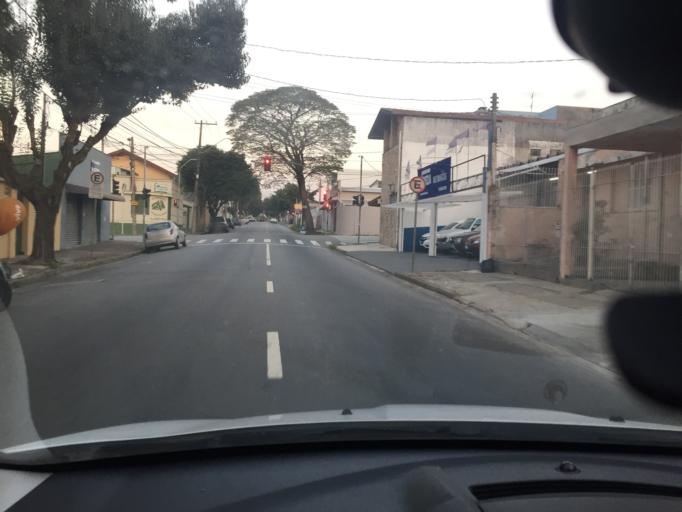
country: BR
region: Sao Paulo
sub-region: Jundiai
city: Jundiai
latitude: -23.2052
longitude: -46.8685
